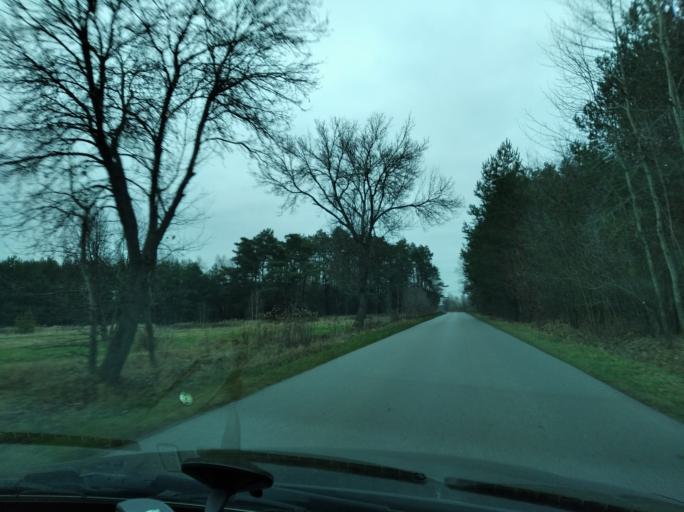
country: PL
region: Subcarpathian Voivodeship
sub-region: Powiat lancucki
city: Rakszawa
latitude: 50.1815
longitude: 22.2468
